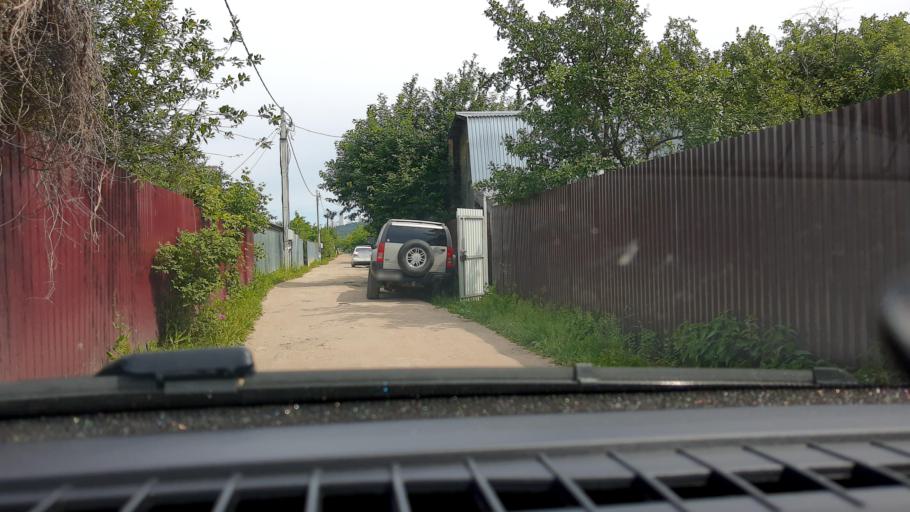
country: RU
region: Nizjnij Novgorod
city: Nizhniy Novgorod
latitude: 56.2663
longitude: 43.9538
